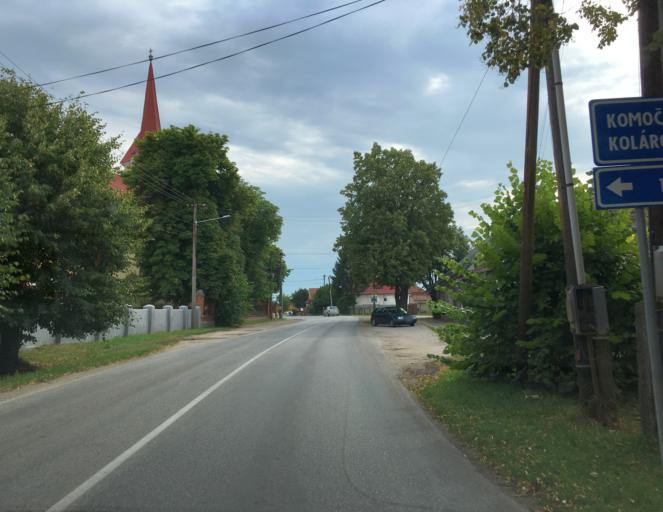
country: SK
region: Nitriansky
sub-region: Okres Nove Zamky
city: Nove Zamky
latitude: 47.9258
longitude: 18.1192
